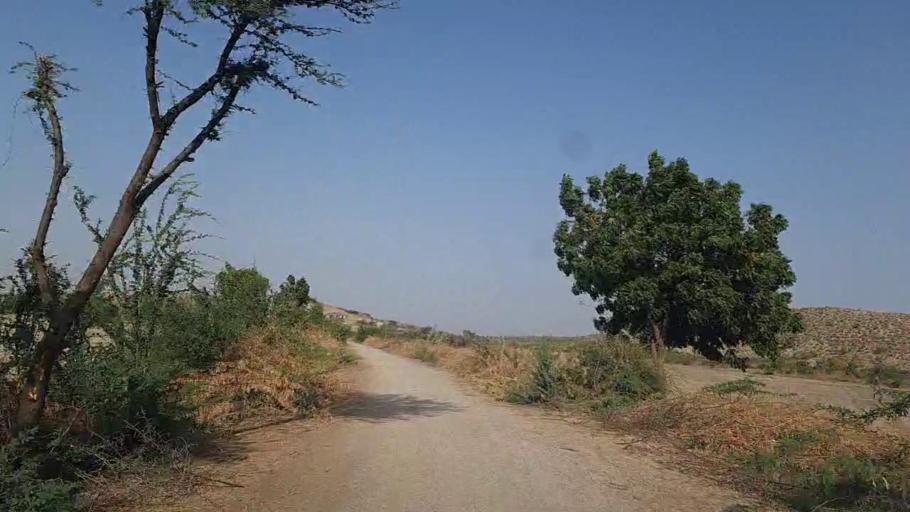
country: PK
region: Sindh
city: Naukot
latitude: 24.5951
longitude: 69.3139
